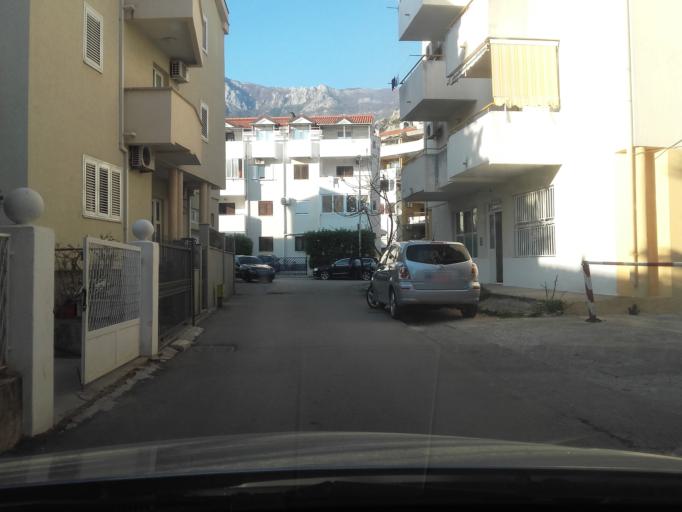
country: ME
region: Budva
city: Budva
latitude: 42.2898
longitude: 18.8480
